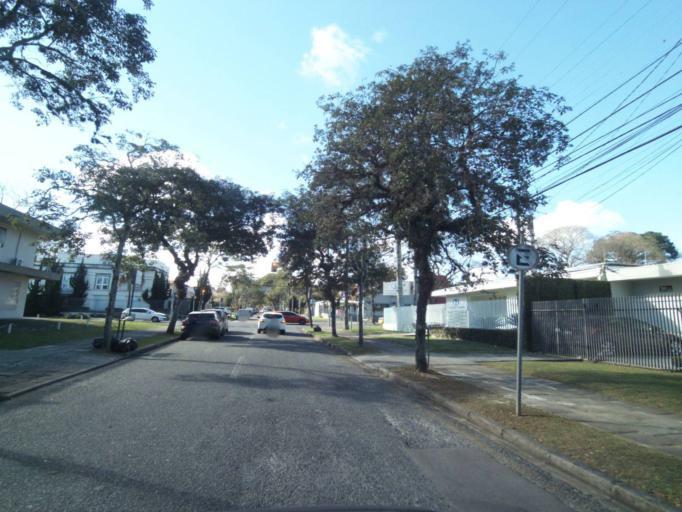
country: BR
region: Parana
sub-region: Curitiba
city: Curitiba
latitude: -25.4186
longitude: -49.2485
